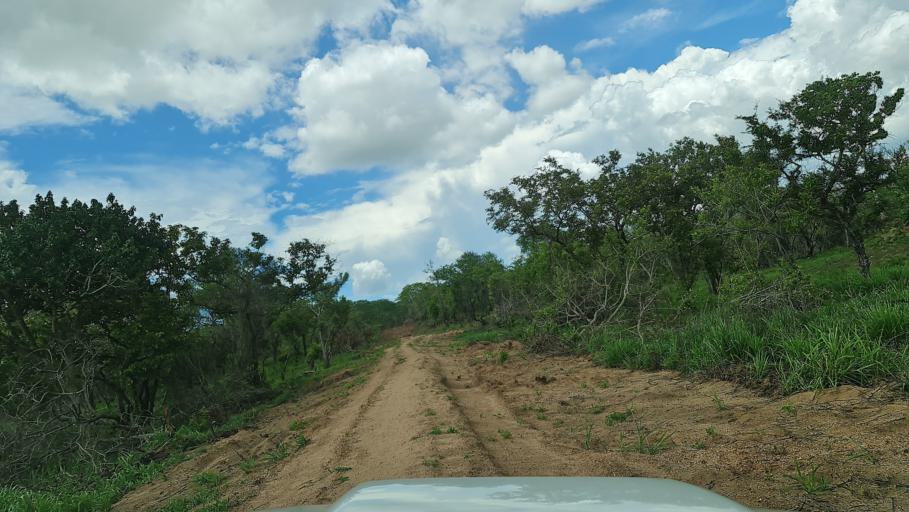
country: MZ
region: Nampula
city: Ilha de Mocambique
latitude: -15.5081
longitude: 40.1900
